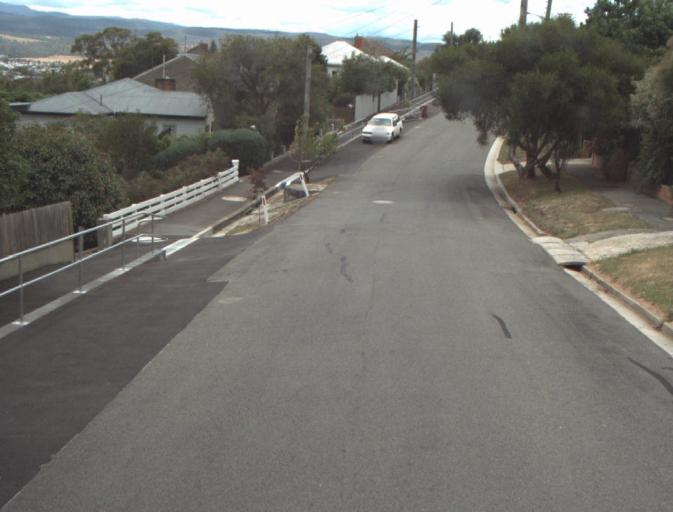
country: AU
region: Tasmania
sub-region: Launceston
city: Launceston
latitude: -41.4375
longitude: 147.1176
